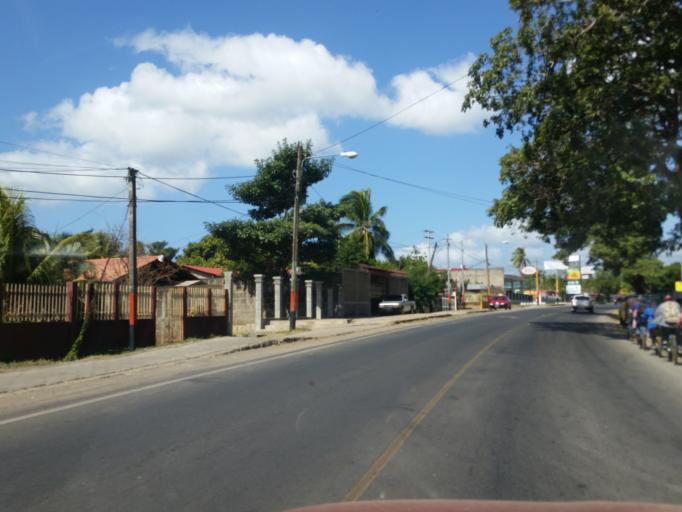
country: NI
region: Granada
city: Nandaime
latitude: 11.7554
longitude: -86.0448
